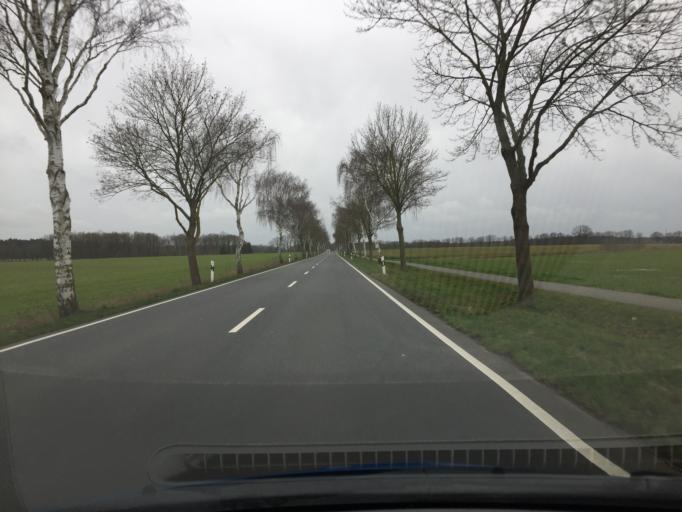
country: DE
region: Lower Saxony
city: Ratzlingen
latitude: 52.9935
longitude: 10.6437
